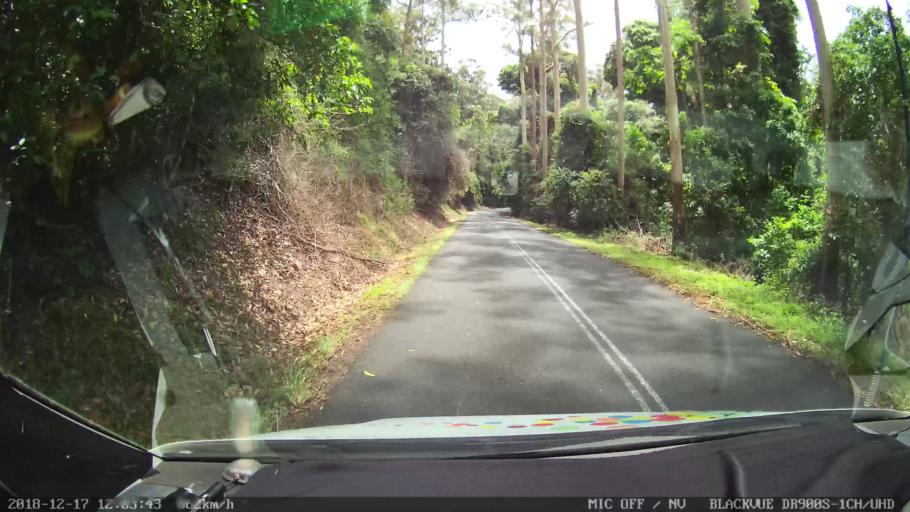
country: AU
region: New South Wales
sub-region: Kyogle
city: Kyogle
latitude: -28.5056
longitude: 152.5680
